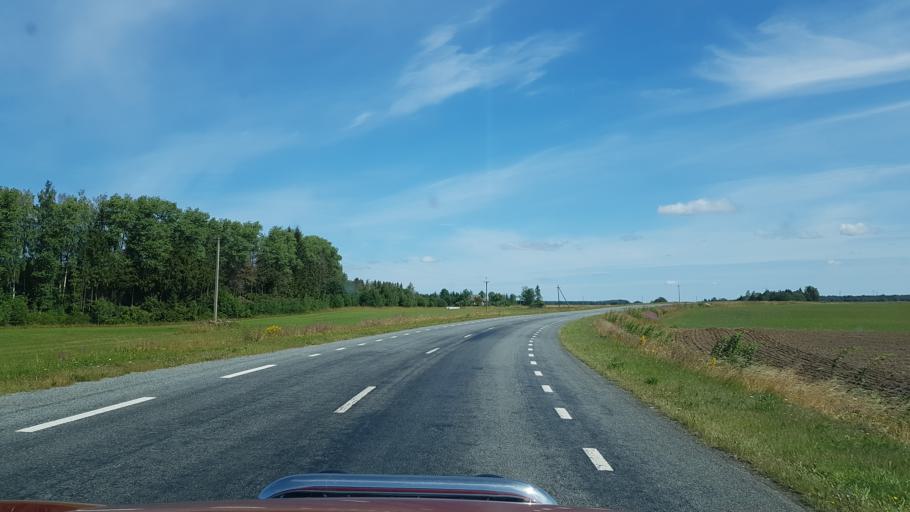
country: EE
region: Jaervamaa
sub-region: Jaerva-Jaani vald
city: Jarva-Jaani
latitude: 59.0688
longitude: 25.9341
